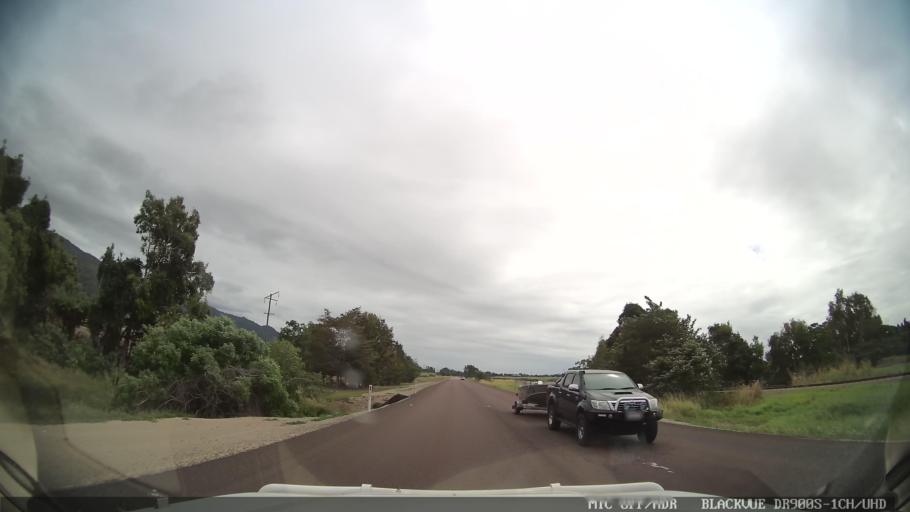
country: AU
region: Queensland
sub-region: Hinchinbrook
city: Ingham
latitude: -18.9238
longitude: 146.2612
